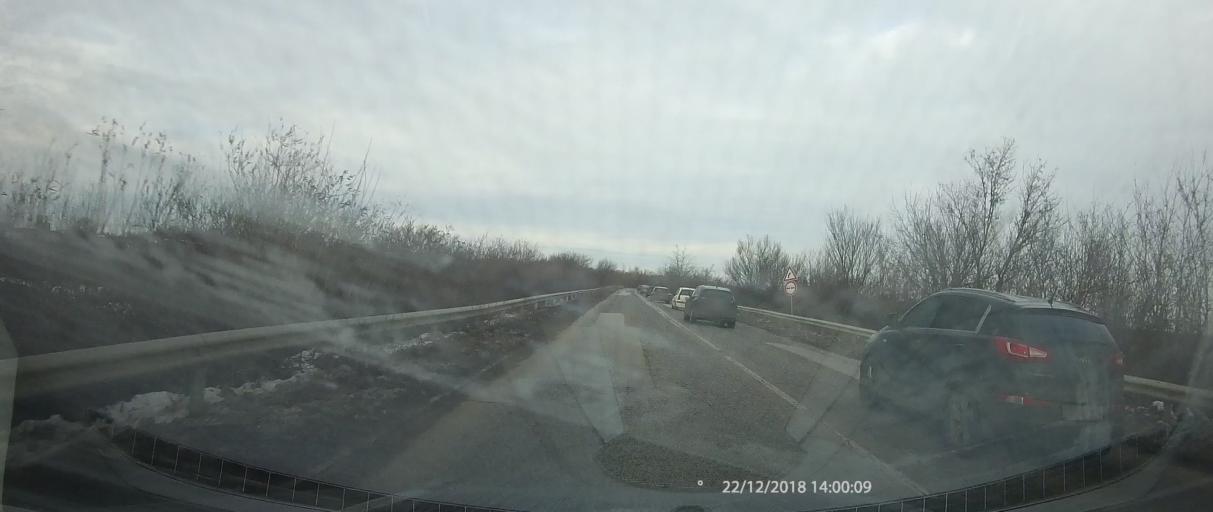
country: BG
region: Pleven
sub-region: Obshtina Dolni Dubnik
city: Dolni Dubnik
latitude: 43.3572
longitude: 24.3435
